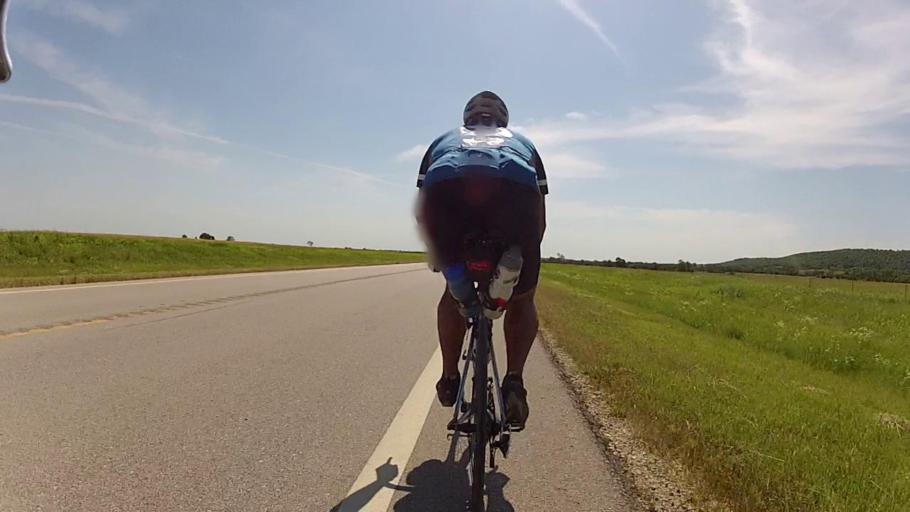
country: US
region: Kansas
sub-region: Chautauqua County
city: Sedan
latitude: 37.1067
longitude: -96.5471
